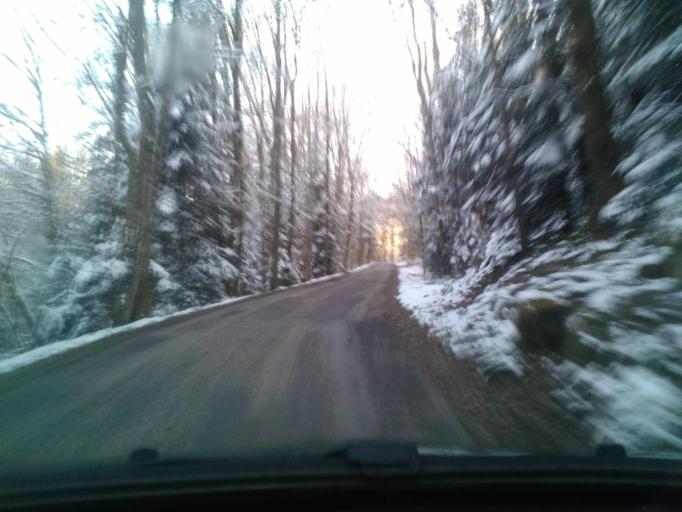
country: FR
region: Lorraine
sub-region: Departement des Vosges
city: Granges-sur-Vologne
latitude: 48.1364
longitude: 6.8218
